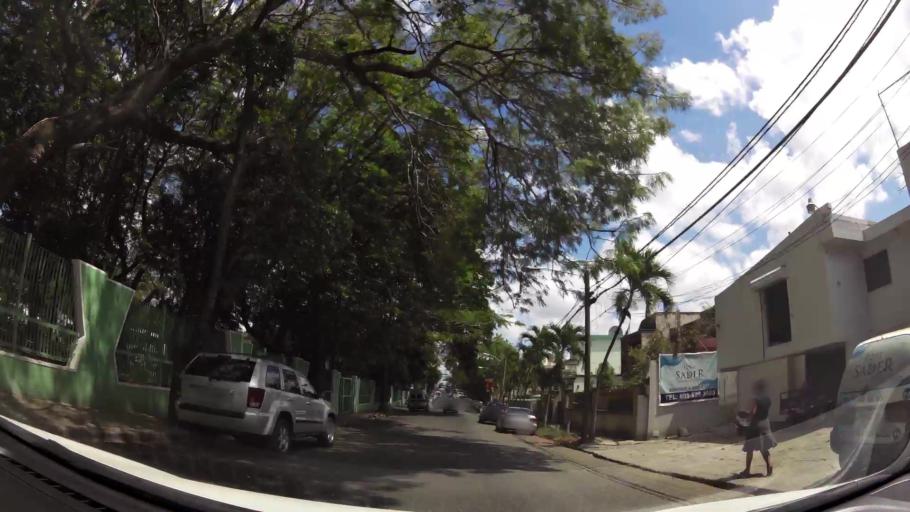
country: DO
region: San Cristobal
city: San Cristobal
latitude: 18.4142
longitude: -70.1122
